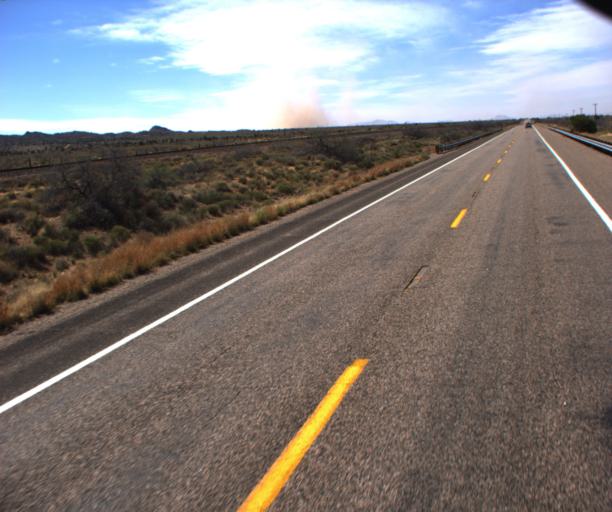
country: US
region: Arizona
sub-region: Mohave County
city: New Kingman-Butler
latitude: 35.4004
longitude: -113.7594
